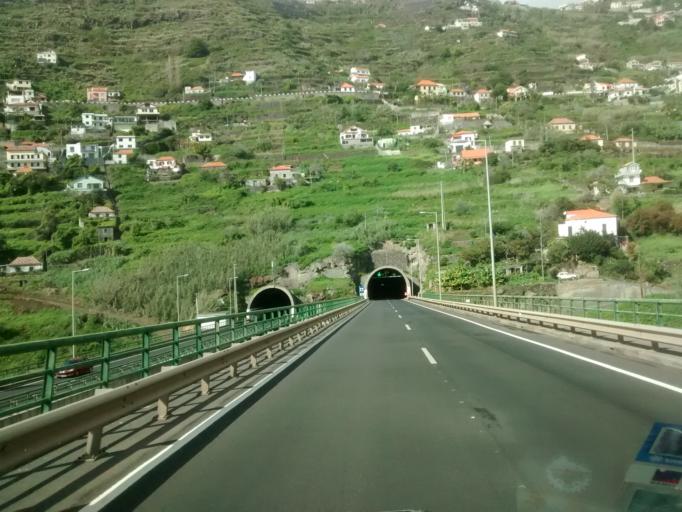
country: PT
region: Madeira
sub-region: Ribeira Brava
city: Campanario
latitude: 32.6680
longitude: -17.0413
